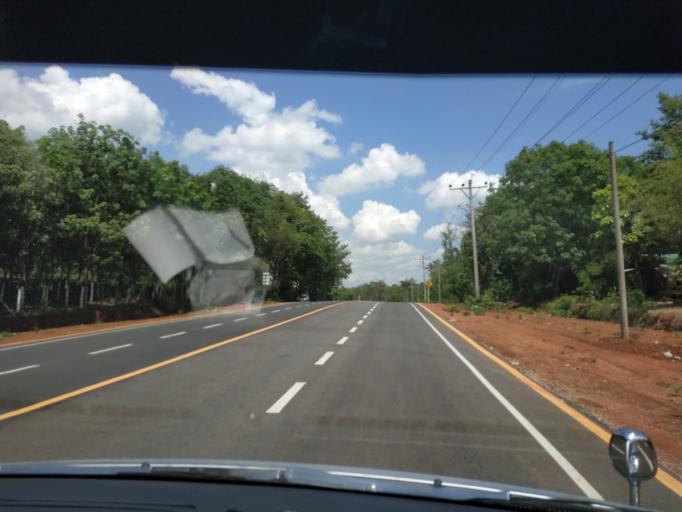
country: MM
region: Mon
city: Kyaikto
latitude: 17.3904
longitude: 97.0669
